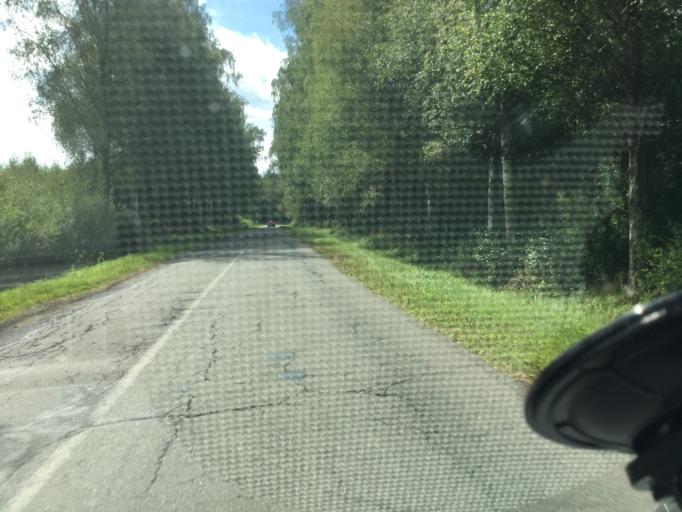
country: BY
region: Vitebsk
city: Chashniki
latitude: 55.3023
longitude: 29.3926
